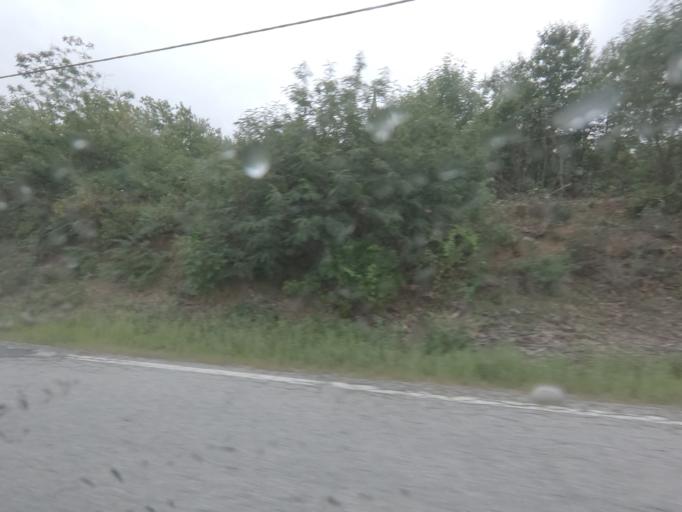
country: PT
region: Viseu
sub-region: Armamar
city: Armamar
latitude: 41.1154
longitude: -7.7185
